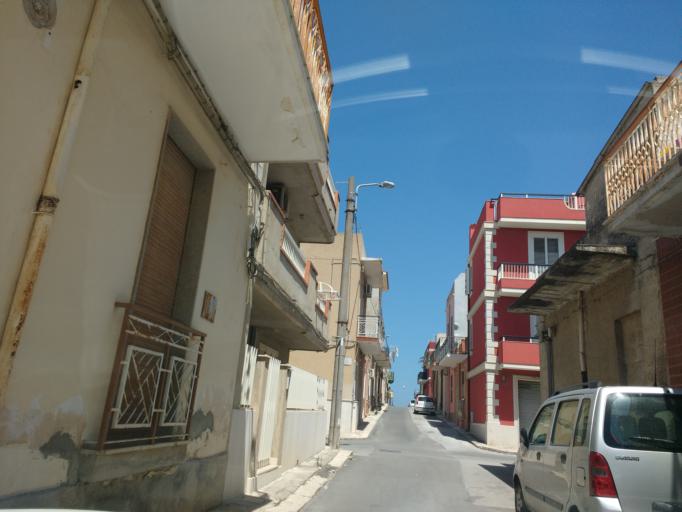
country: IT
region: Sicily
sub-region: Provincia di Siracusa
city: Pachino
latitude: 36.7178
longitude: 15.0971
